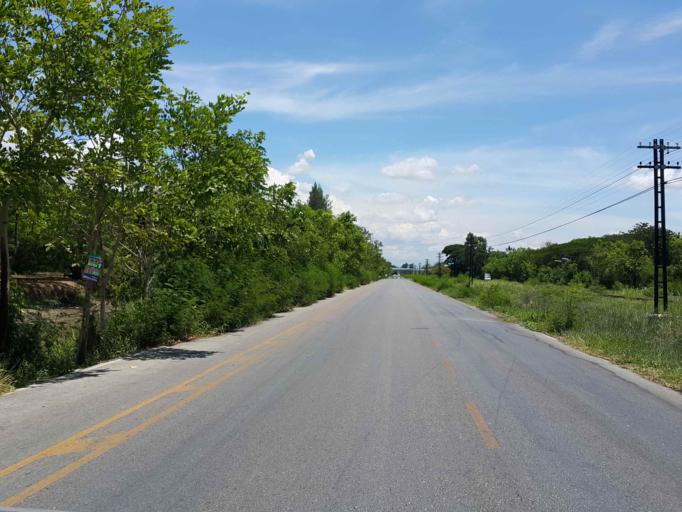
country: TH
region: Chiang Mai
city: Saraphi
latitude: 18.7539
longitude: 99.0228
